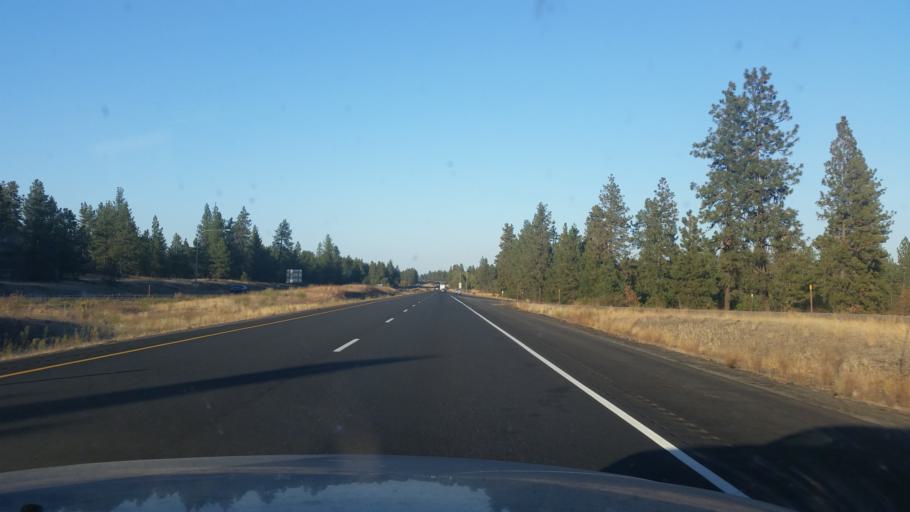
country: US
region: Washington
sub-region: Spokane County
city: Medical Lake
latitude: 47.5052
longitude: -117.6893
